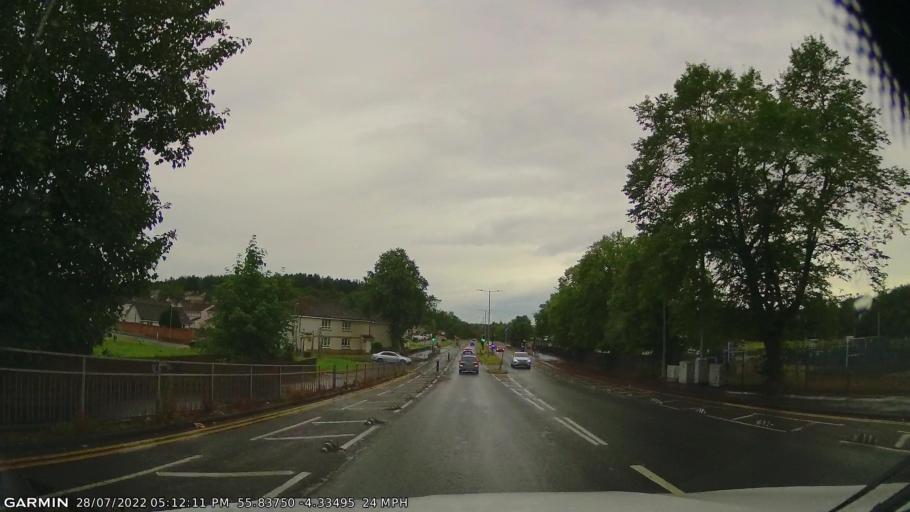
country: GB
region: Scotland
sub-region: East Renfrewshire
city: Giffnock
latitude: 55.8375
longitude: -4.3350
